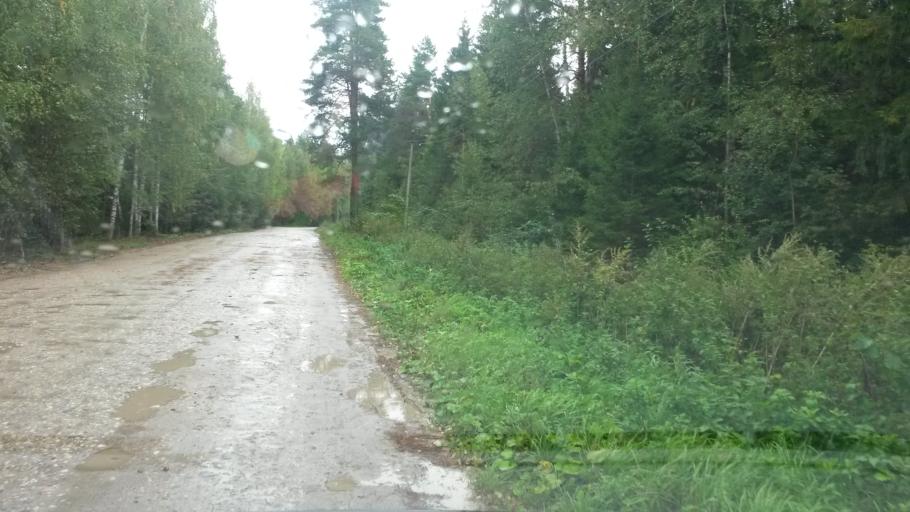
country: RU
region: Ivanovo
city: Zarechnyy
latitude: 57.5035
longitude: 42.3001
